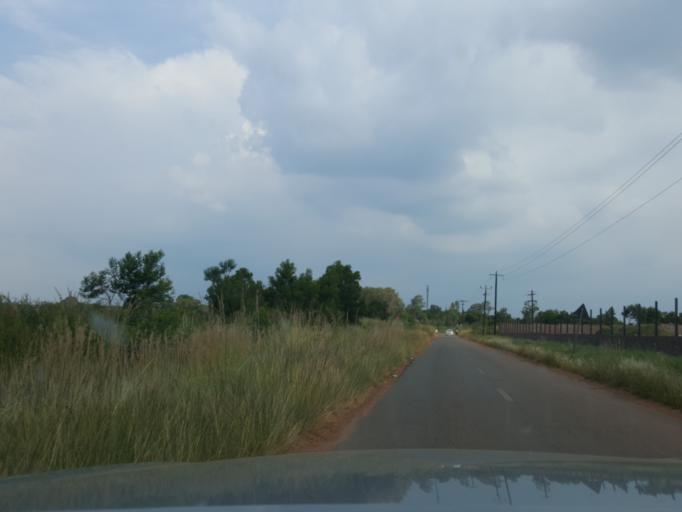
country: ZA
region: Gauteng
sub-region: City of Tshwane Metropolitan Municipality
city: Centurion
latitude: -25.8612
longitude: 28.3276
